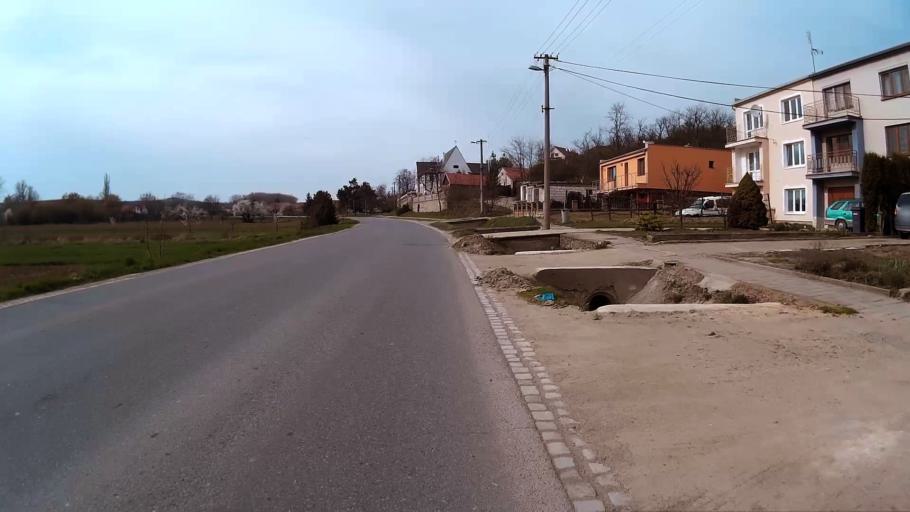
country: CZ
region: South Moravian
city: Dolni Kounice
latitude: 49.0528
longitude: 16.4906
